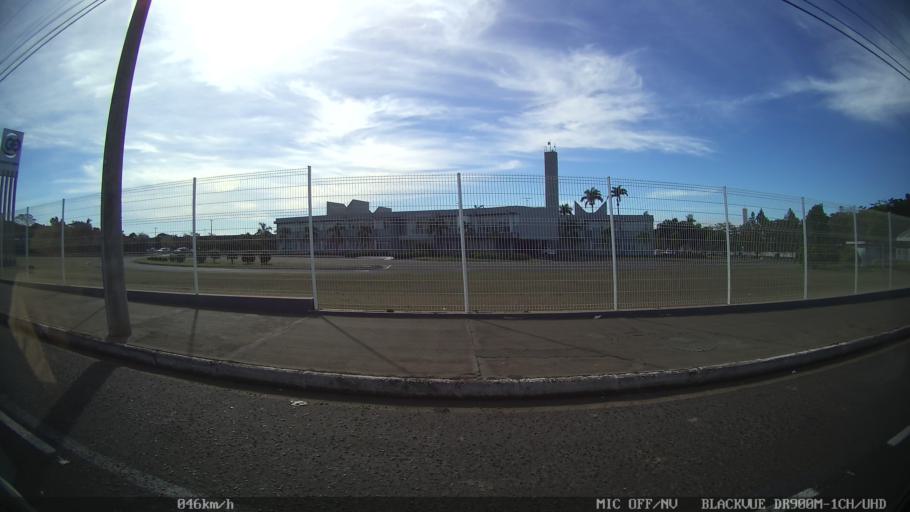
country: BR
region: Sao Paulo
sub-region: Sao Jose Do Rio Preto
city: Sao Jose do Rio Preto
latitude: -20.7999
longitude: -49.3368
